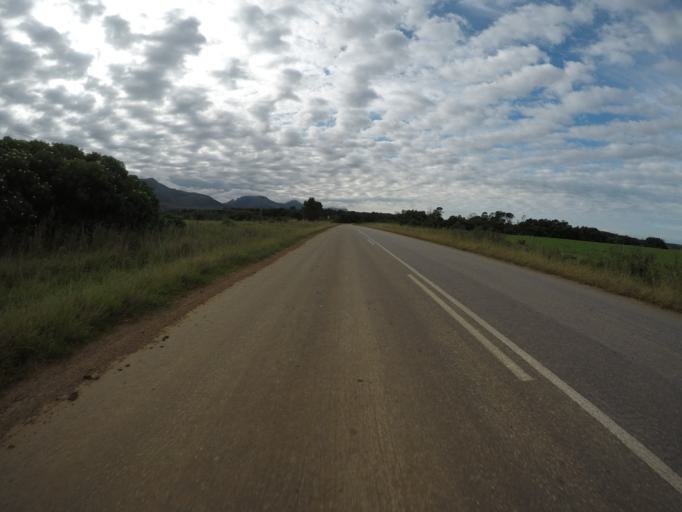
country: ZA
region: Eastern Cape
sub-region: Cacadu District Municipality
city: Kareedouw
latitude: -34.0119
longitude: 24.2935
